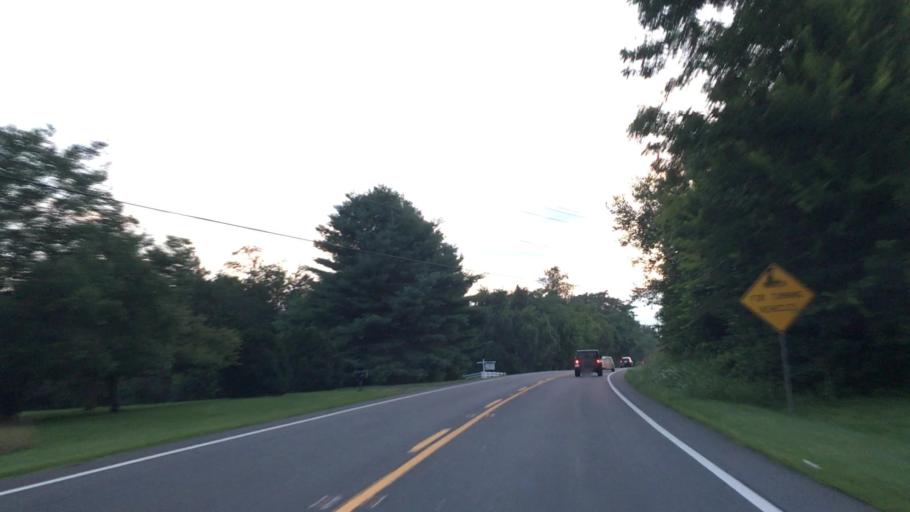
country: US
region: Virginia
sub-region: Orange County
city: Orange
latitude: 38.2438
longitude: -78.0731
